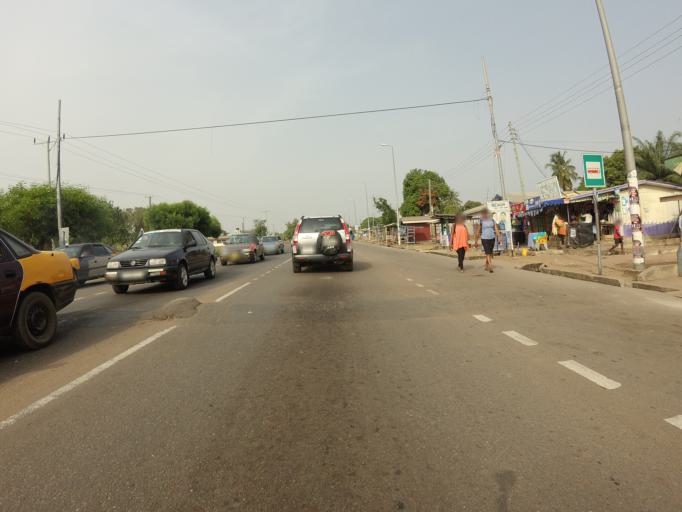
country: GH
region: Volta
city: Ho
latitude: 6.6035
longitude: 0.4842
